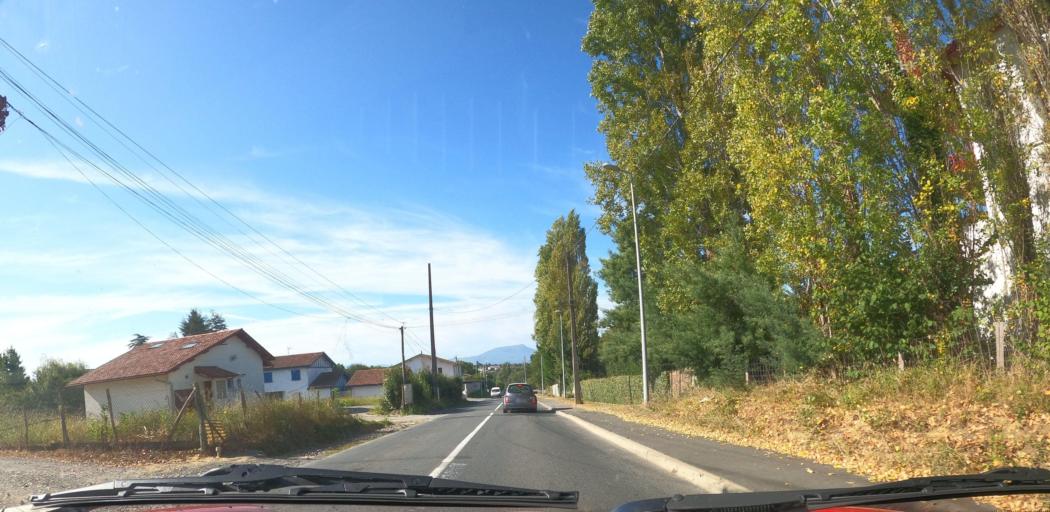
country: FR
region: Aquitaine
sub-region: Departement des Pyrenees-Atlantiques
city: Arbonne
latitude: 43.4431
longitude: -1.5454
